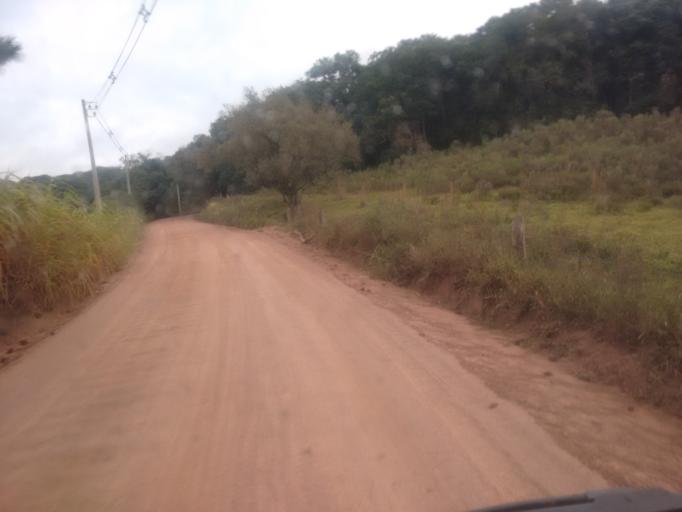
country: BR
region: Rio Grande do Sul
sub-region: Camaqua
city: Camaqua
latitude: -30.7298
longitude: -51.8417
